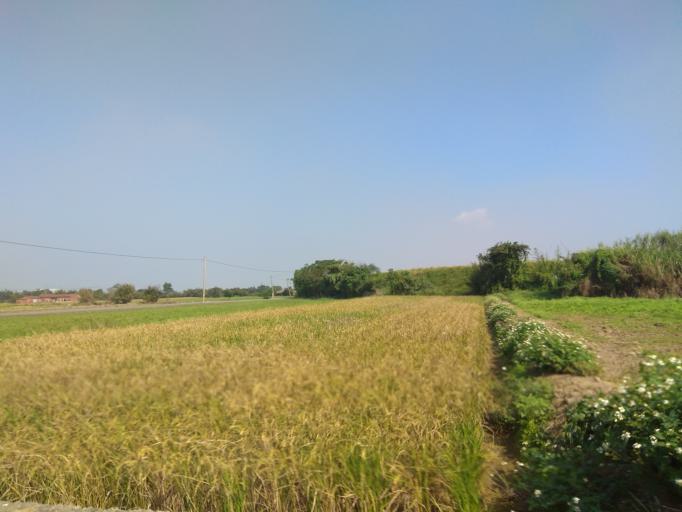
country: TW
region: Taiwan
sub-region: Hsinchu
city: Zhubei
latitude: 24.9932
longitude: 121.0682
